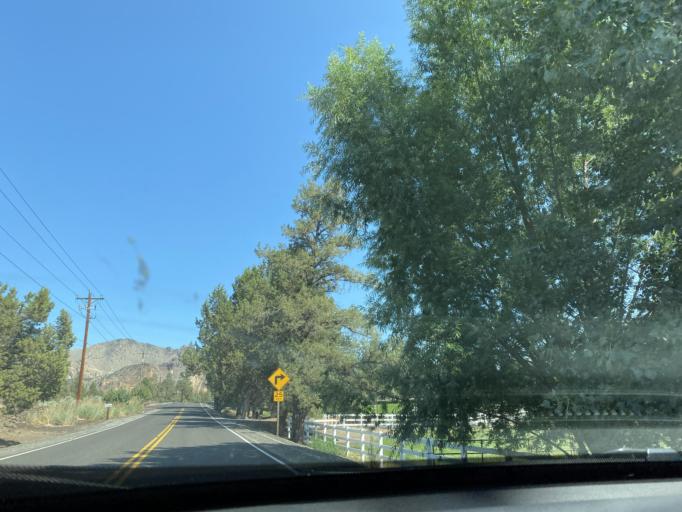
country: US
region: Oregon
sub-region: Deschutes County
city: Terrebonne
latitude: 44.3704
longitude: -121.1665
